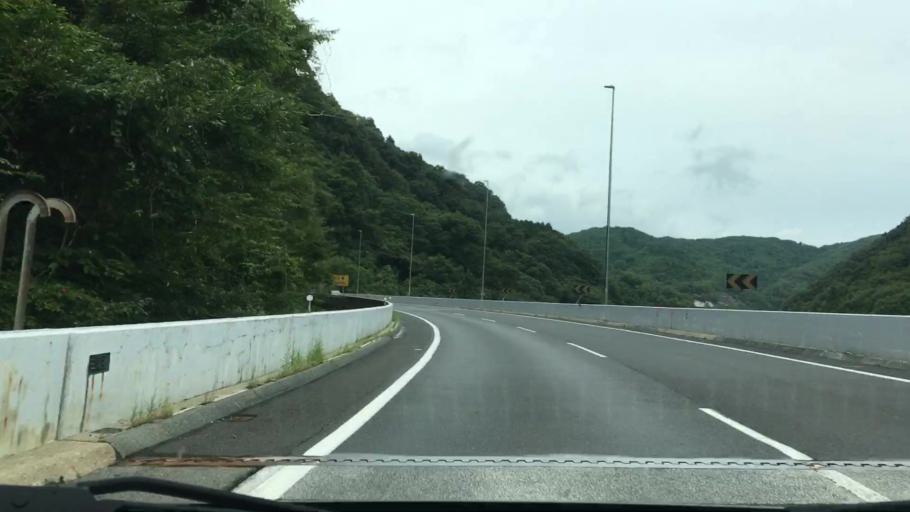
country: JP
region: Okayama
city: Niimi
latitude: 34.9958
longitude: 133.6052
